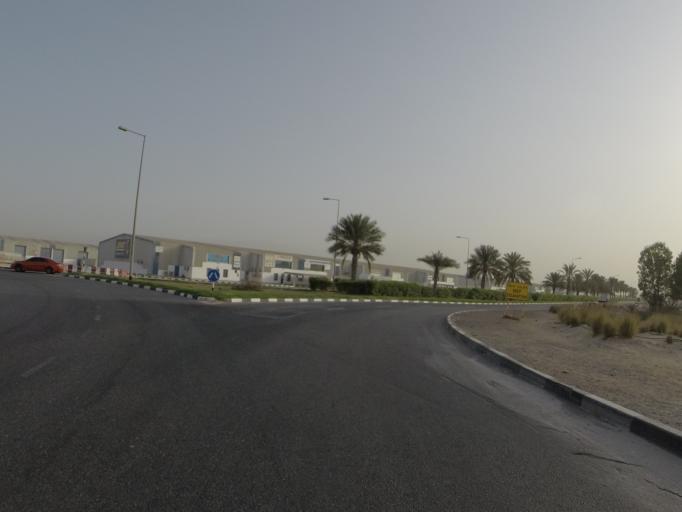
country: AE
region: Dubai
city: Dubai
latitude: 24.9571
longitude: 55.0620
